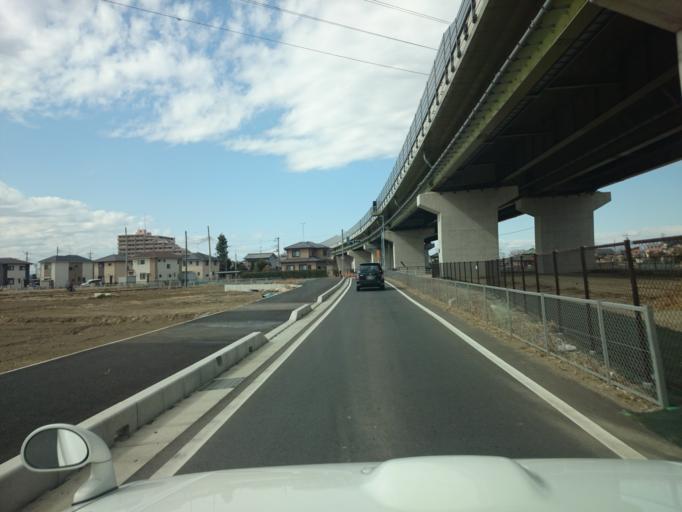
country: JP
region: Saitama
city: Satte
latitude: 36.0642
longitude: 139.7108
